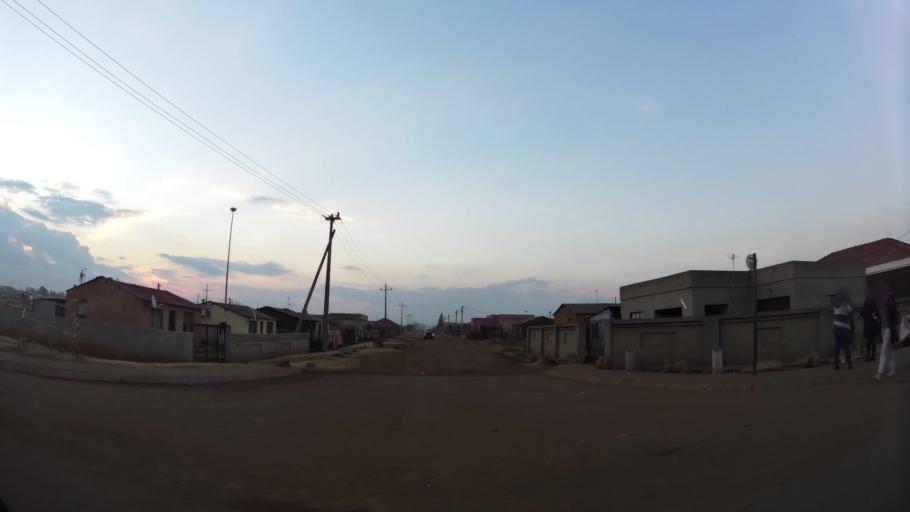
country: ZA
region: Gauteng
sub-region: City of Johannesburg Metropolitan Municipality
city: Orange Farm
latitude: -26.5563
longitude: 27.8743
